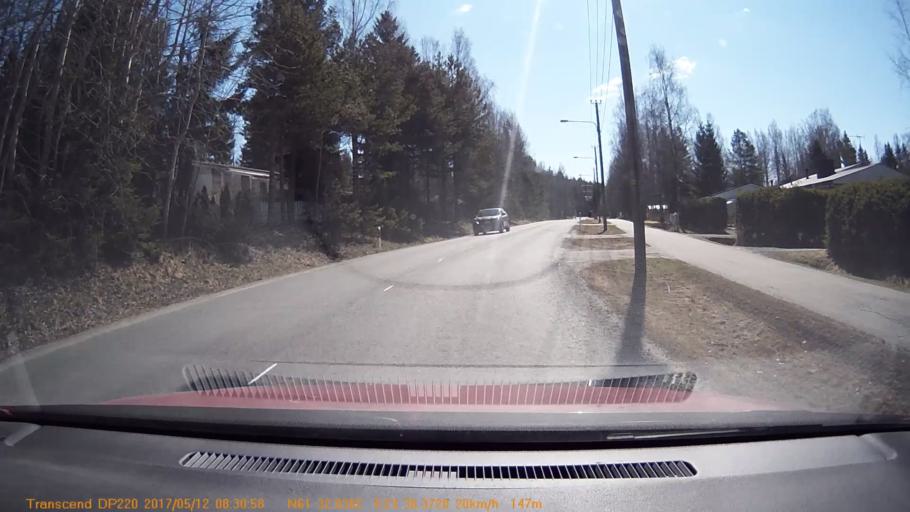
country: FI
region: Pirkanmaa
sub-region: Tampere
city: Yloejaervi
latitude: 61.5340
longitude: 23.6062
